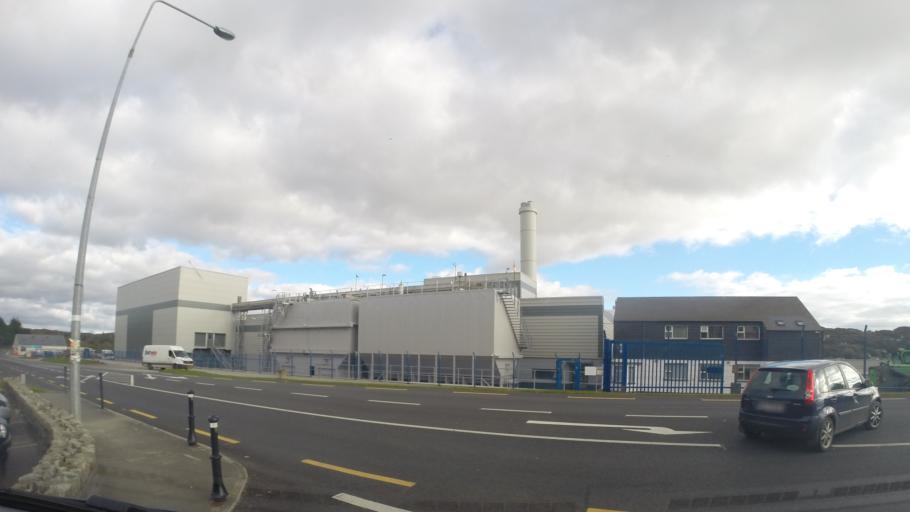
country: IE
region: Ulster
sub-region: County Donegal
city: Killybegs
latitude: 54.6451
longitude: -8.4318
